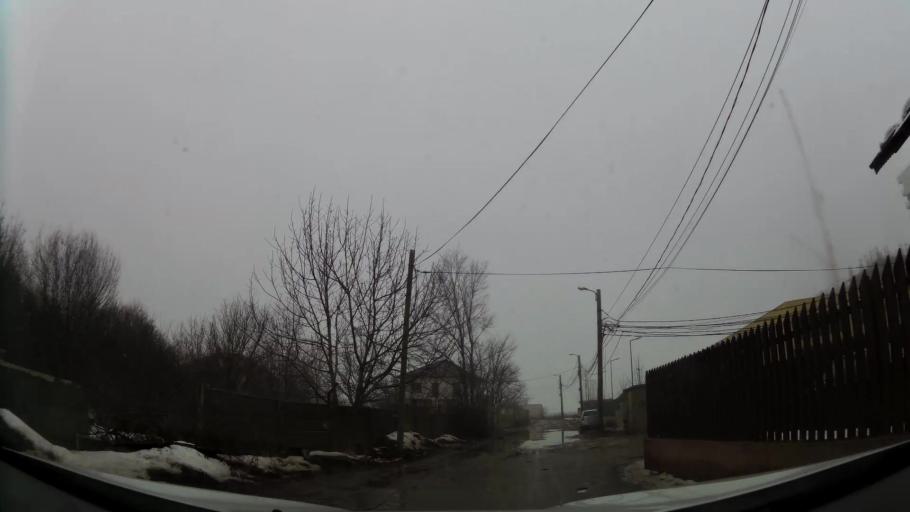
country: RO
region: Ilfov
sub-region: Comuna Chiajna
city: Rosu
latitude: 44.4473
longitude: 26.0208
